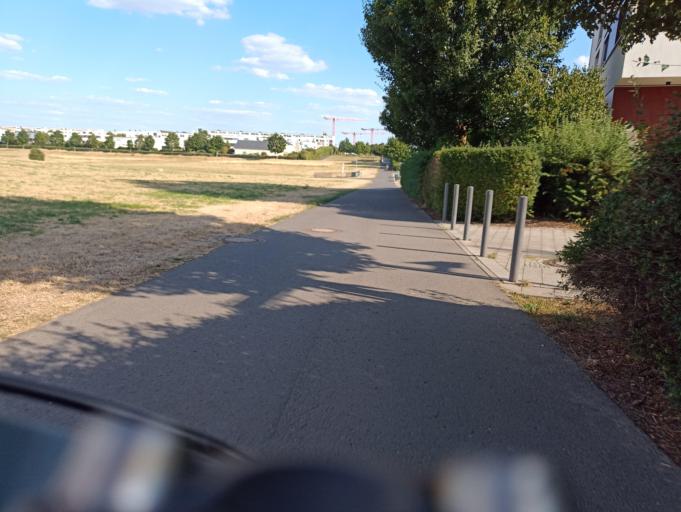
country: DE
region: Hesse
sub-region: Regierungsbezirk Darmstadt
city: Bad Homburg vor der Hoehe
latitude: 50.1814
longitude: 8.6287
